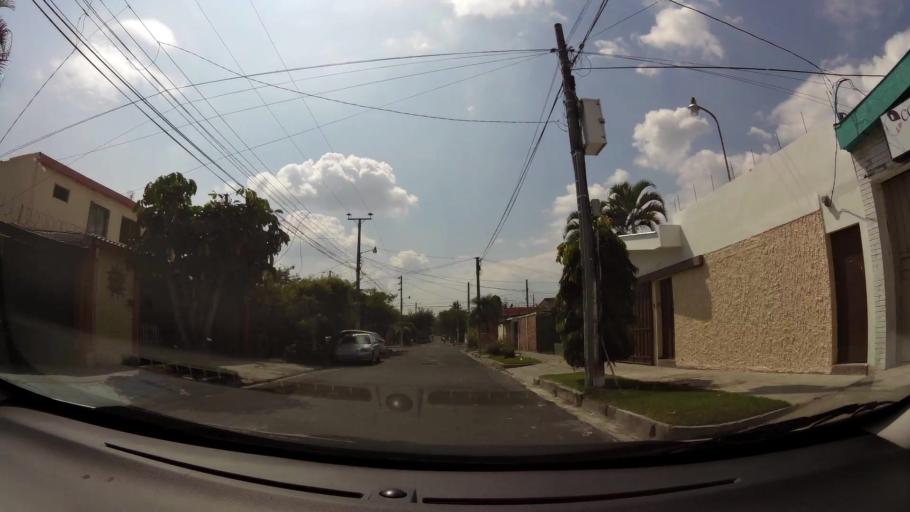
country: SV
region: San Salvador
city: Mejicanos
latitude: 13.7131
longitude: -89.2217
